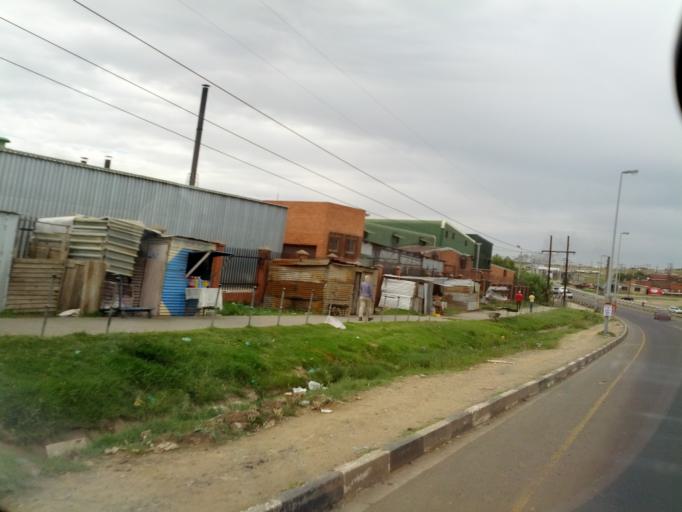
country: LS
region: Maseru
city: Maseru
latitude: -29.3427
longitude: 27.4591
